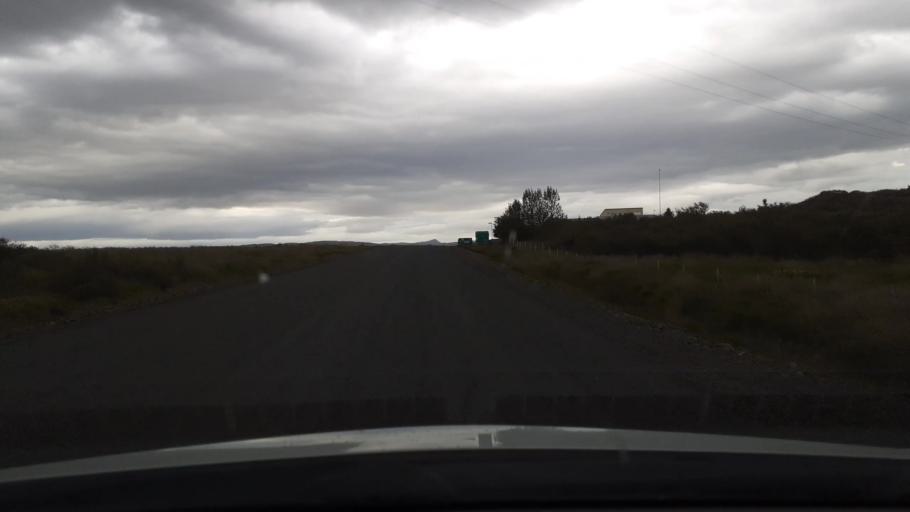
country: IS
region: West
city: Borgarnes
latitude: 64.6729
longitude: -21.7040
